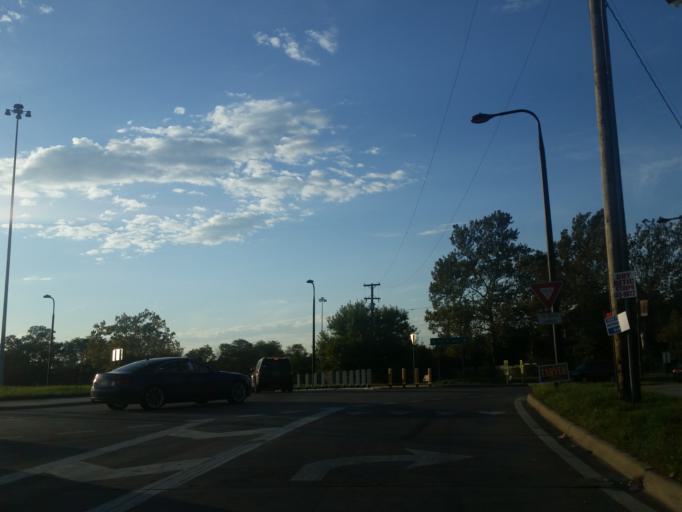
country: US
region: Ohio
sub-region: Cuyahoga County
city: Newburgh Heights
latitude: 41.4662
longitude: -81.6907
